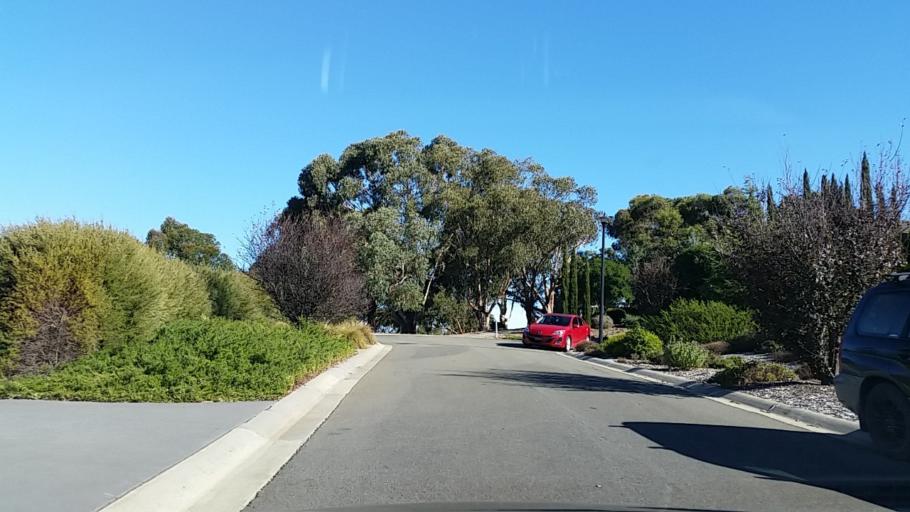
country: AU
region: South Australia
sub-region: Mount Barker
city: Mount Barker
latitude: -35.0589
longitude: 138.8834
